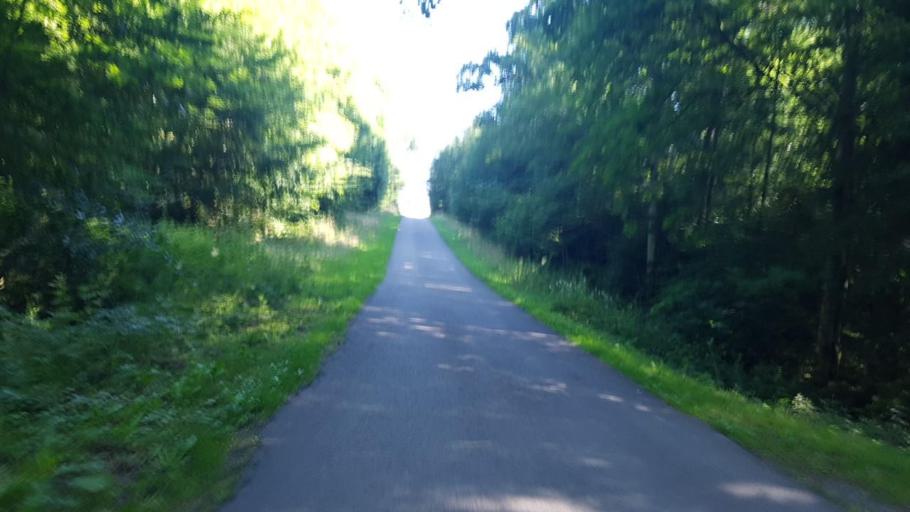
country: FR
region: Nord-Pas-de-Calais
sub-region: Departement du Nord
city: Anor
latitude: 49.9602
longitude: 4.1105
